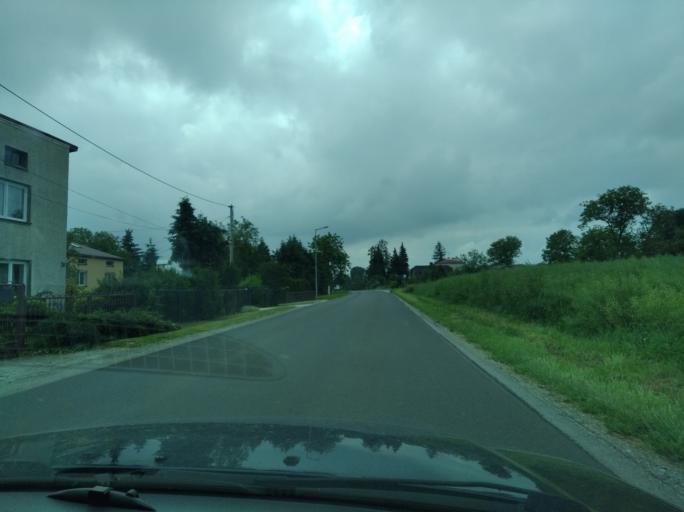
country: PL
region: Subcarpathian Voivodeship
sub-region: Powiat jaroslawski
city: Pawlosiow
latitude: 50.0193
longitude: 22.6403
